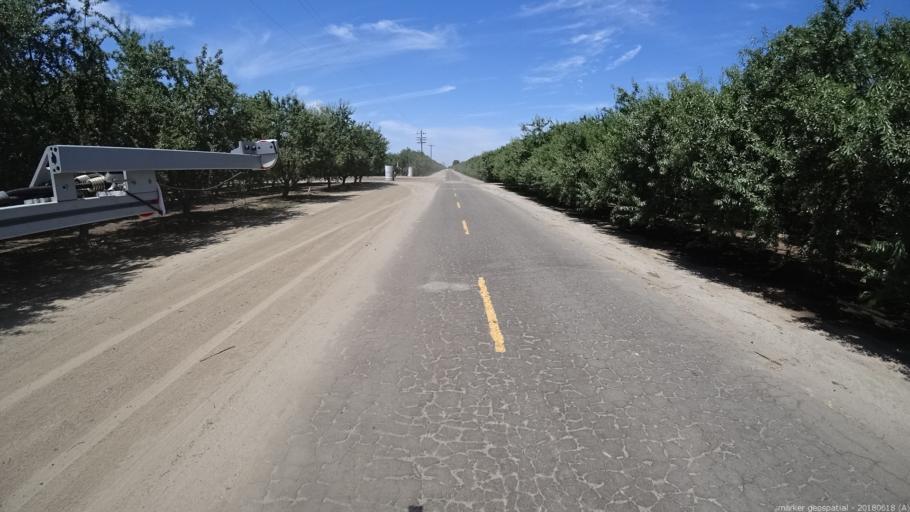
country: US
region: California
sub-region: Madera County
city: Parkwood
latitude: 36.9020
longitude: -120.1325
